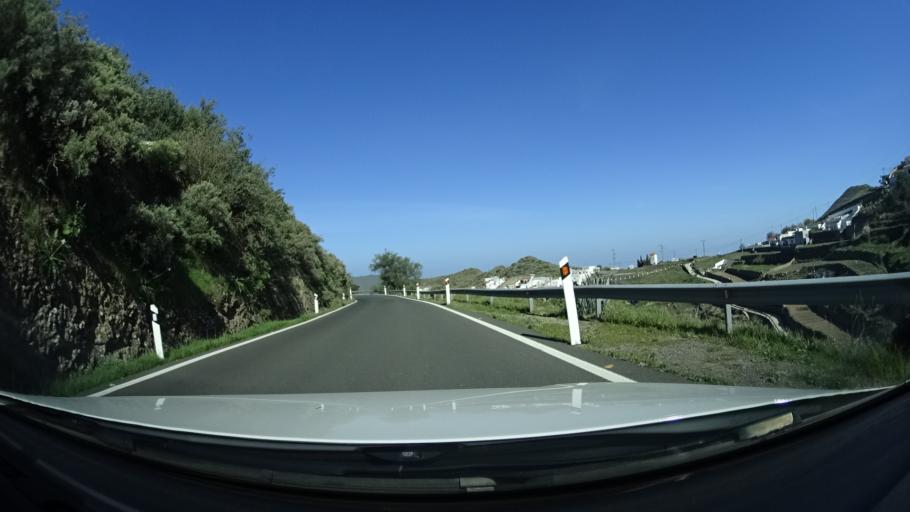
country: ES
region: Canary Islands
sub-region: Provincia de Las Palmas
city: Artenara
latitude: 28.0239
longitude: -15.6351
